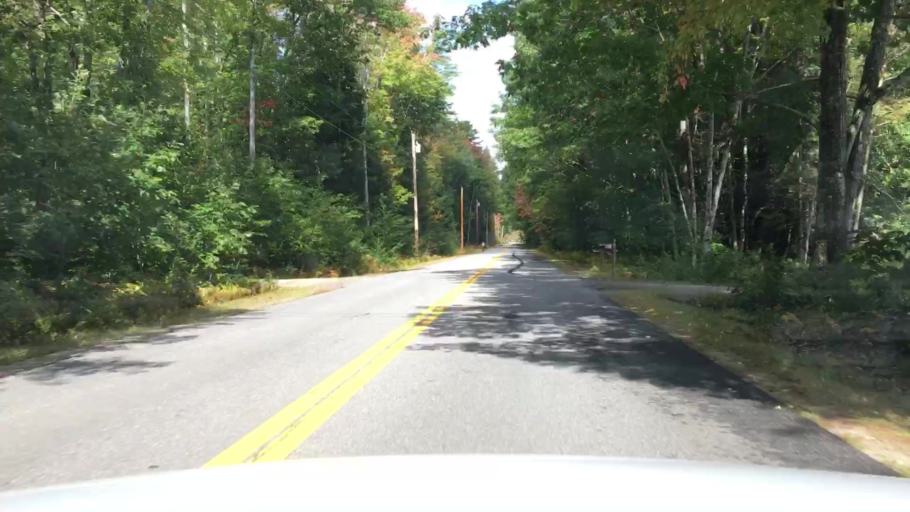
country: US
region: Maine
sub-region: Cumberland County
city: Brunswick
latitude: 43.9578
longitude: -69.8958
